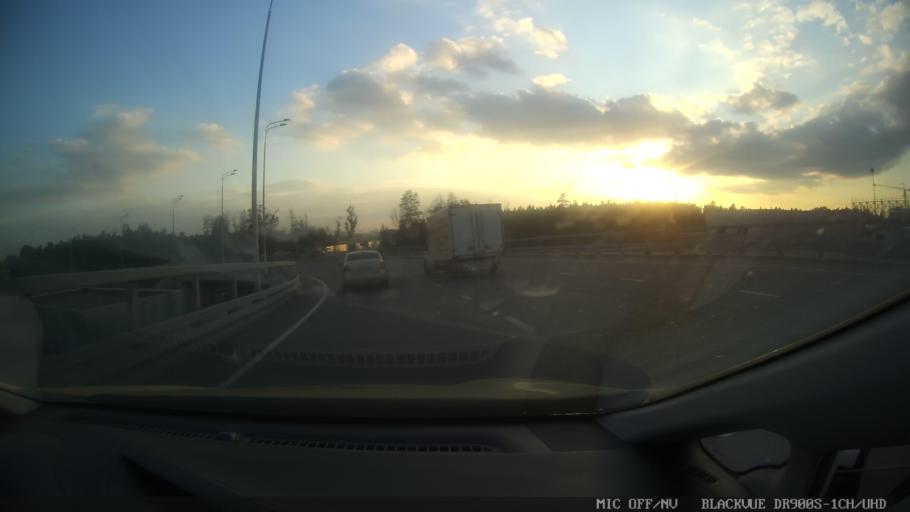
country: RU
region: Moskovskaya
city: Novopodrezkovo
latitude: 55.9614
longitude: 37.4034
